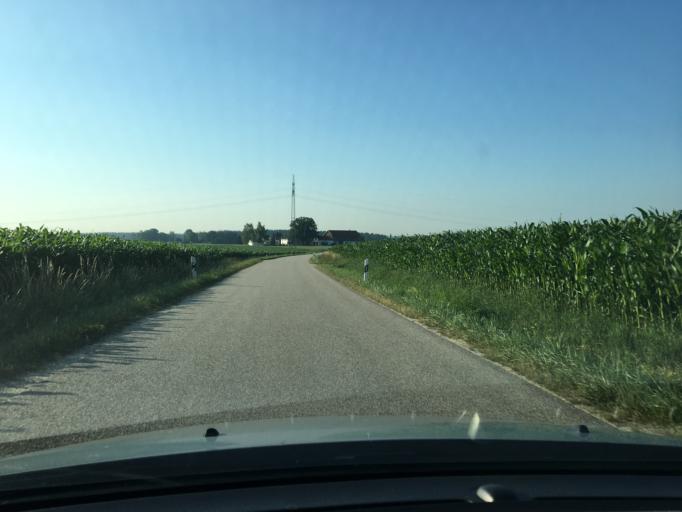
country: DE
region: Bavaria
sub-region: Lower Bavaria
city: Vilsbiburg
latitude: 48.4468
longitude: 12.3031
